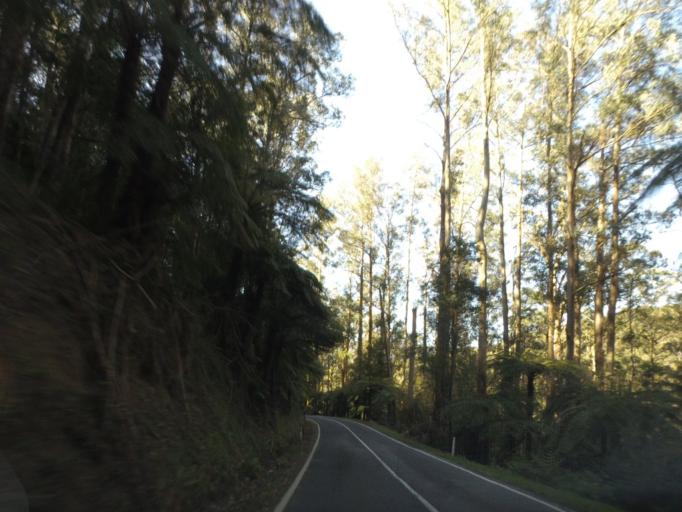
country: AU
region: Victoria
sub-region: Yarra Ranges
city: Millgrove
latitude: -37.8755
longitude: 145.7834
